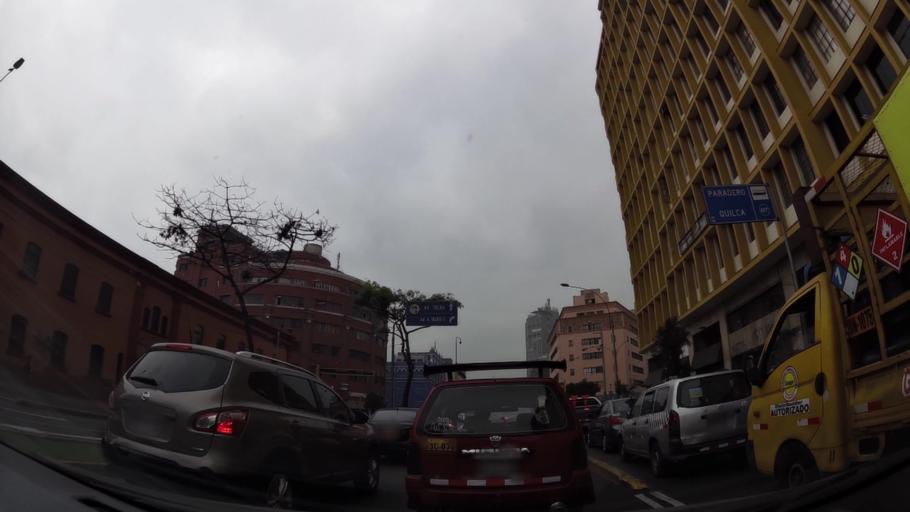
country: PE
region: Lima
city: Lima
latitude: -12.0514
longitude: -77.0386
